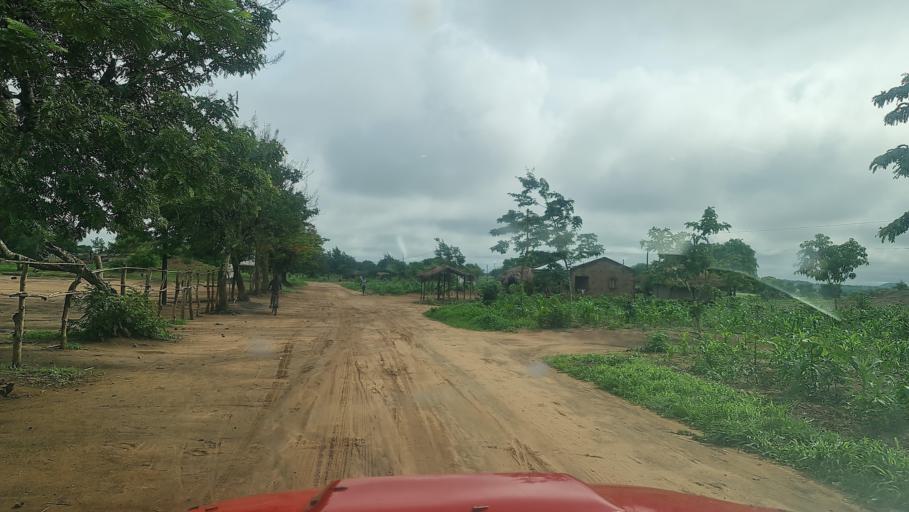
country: MW
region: Southern Region
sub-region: Nsanje District
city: Nsanje
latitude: -17.2205
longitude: 35.6726
